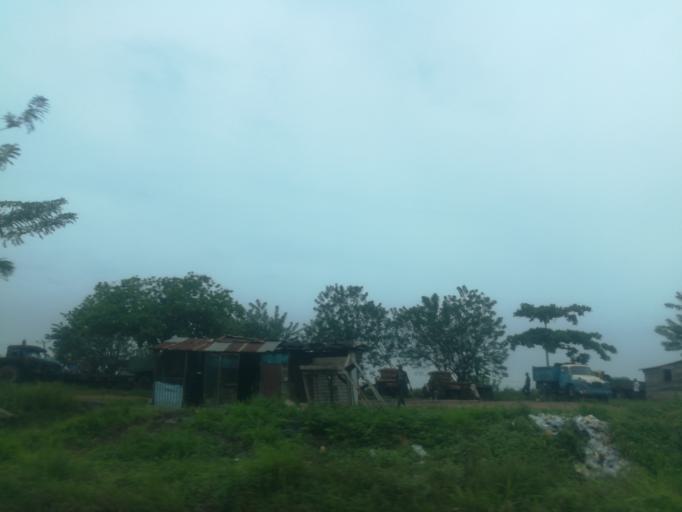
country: NG
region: Oyo
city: Egbeda
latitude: 7.3828
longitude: 4.0116
